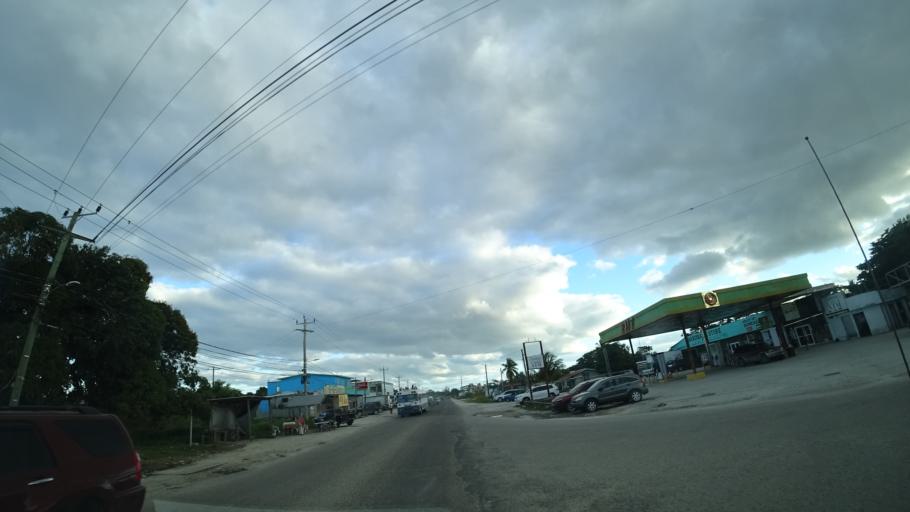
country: BZ
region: Belize
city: Belize City
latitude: 17.5554
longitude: -88.3090
